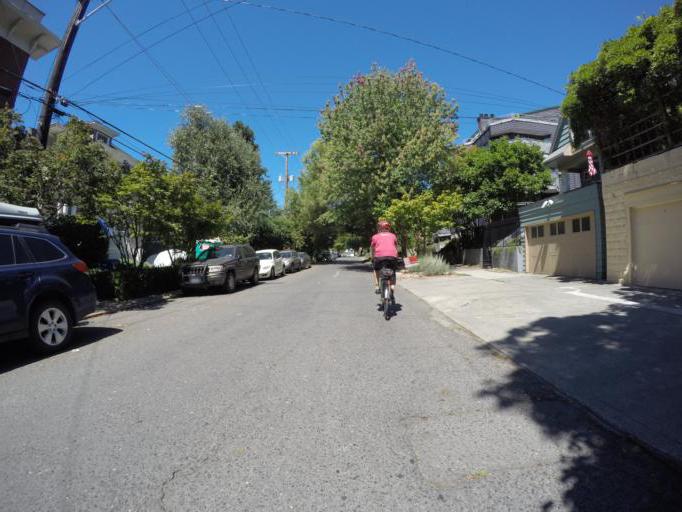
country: US
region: Washington
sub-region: King County
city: Seattle
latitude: 47.6190
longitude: -122.3182
